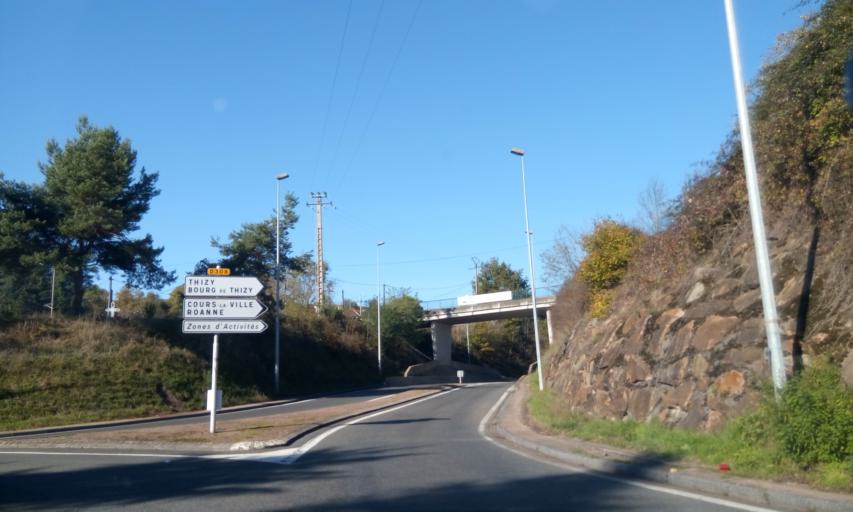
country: FR
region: Rhone-Alpes
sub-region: Departement du Rhone
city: Thizy-les-Bourgs
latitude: 46.0189
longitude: 4.3148
